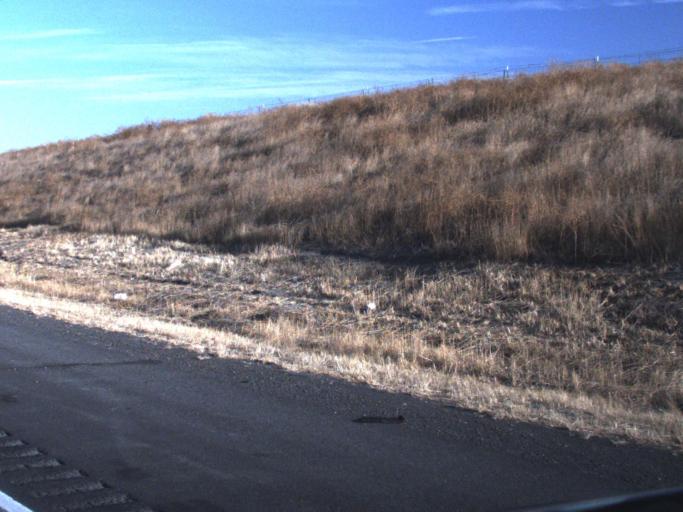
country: US
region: Washington
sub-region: Yakima County
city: Granger
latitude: 46.3574
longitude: -120.1998
